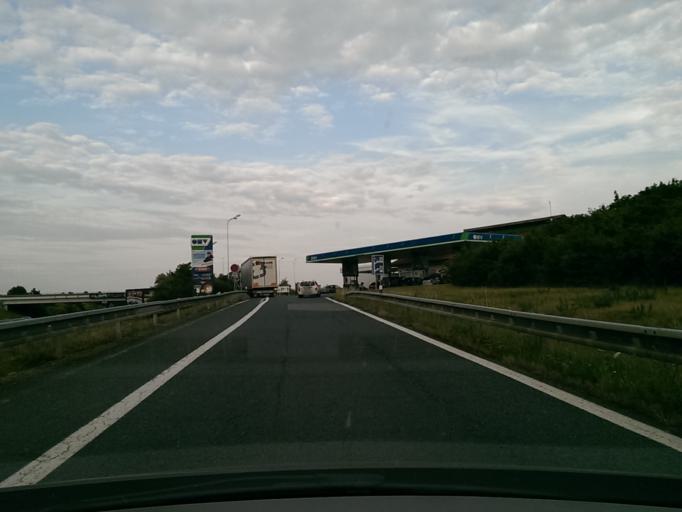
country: CZ
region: South Moravian
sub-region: Mesto Brno
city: Brno
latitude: 49.1631
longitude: 16.6592
